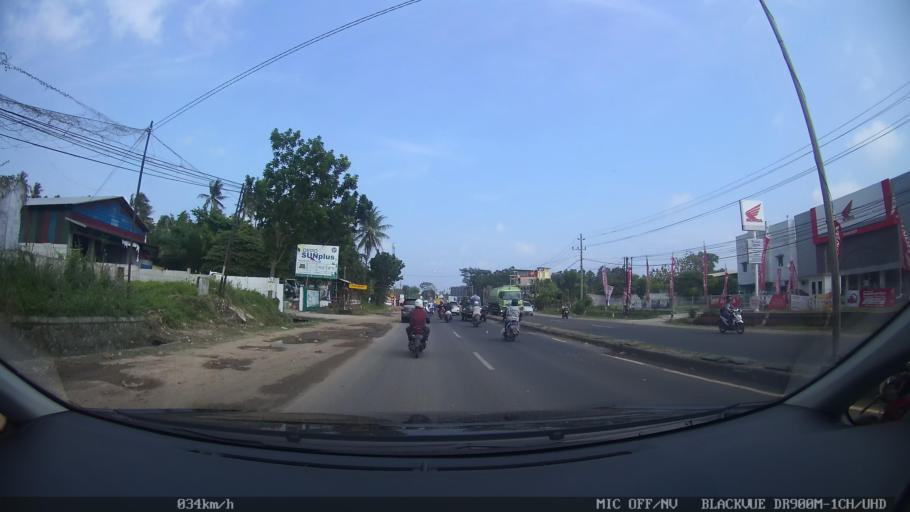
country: ID
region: Lampung
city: Kedaton
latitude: -5.3655
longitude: 105.2650
